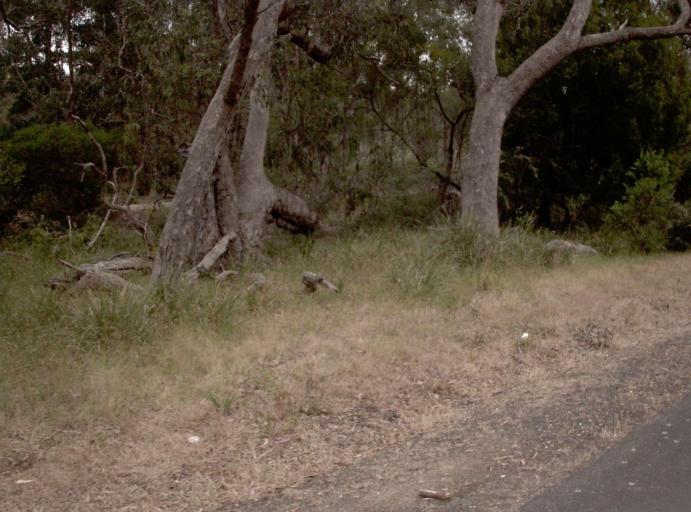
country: AU
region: Victoria
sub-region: Wellington
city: Sale
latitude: -38.2506
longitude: 147.0522
